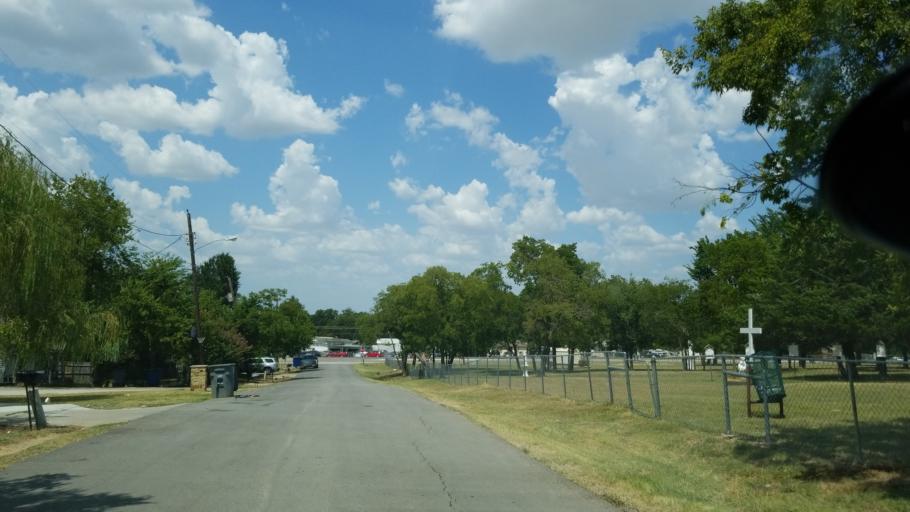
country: US
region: Texas
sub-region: Dallas County
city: Cockrell Hill
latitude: 32.7426
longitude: -96.9060
